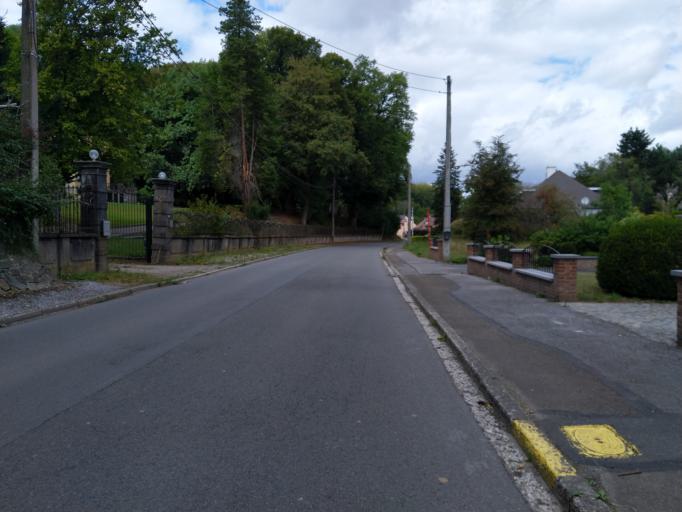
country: BE
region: Wallonia
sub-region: Province du Hainaut
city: Thuin
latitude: 50.3809
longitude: 4.3495
